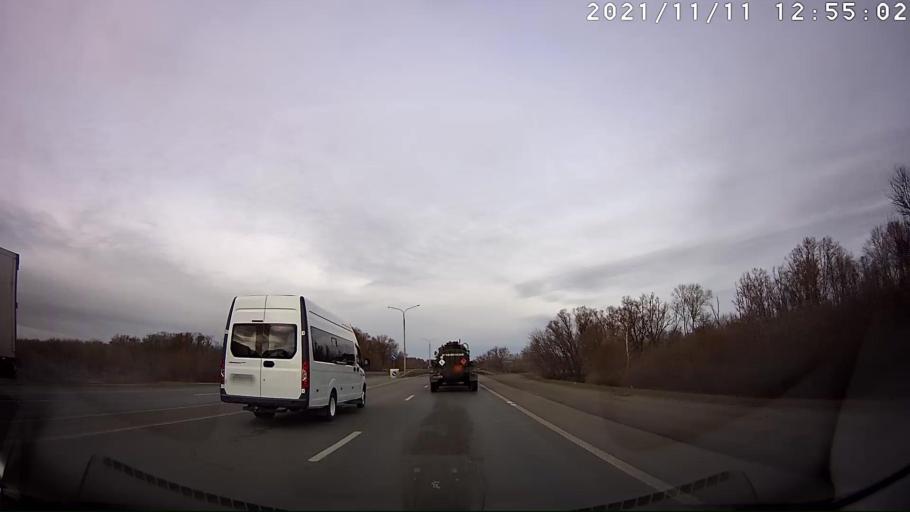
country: RU
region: Ulyanovsk
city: Isheyevka
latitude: 54.3021
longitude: 48.2437
